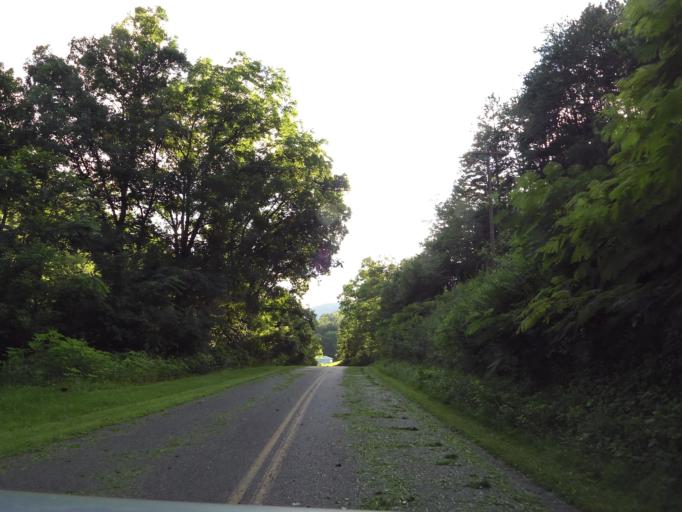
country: US
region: Tennessee
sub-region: Blount County
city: Maryville
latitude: 35.6076
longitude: -83.9613
